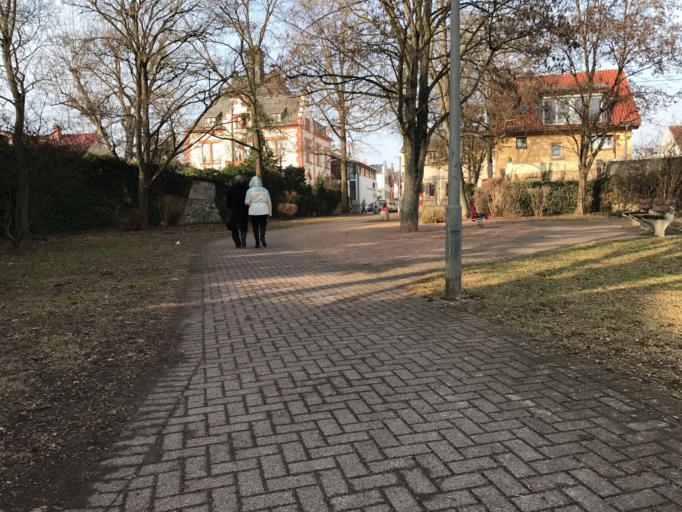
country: DE
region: Rheinland-Pfalz
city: Budenheim
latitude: 50.0451
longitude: 8.1962
